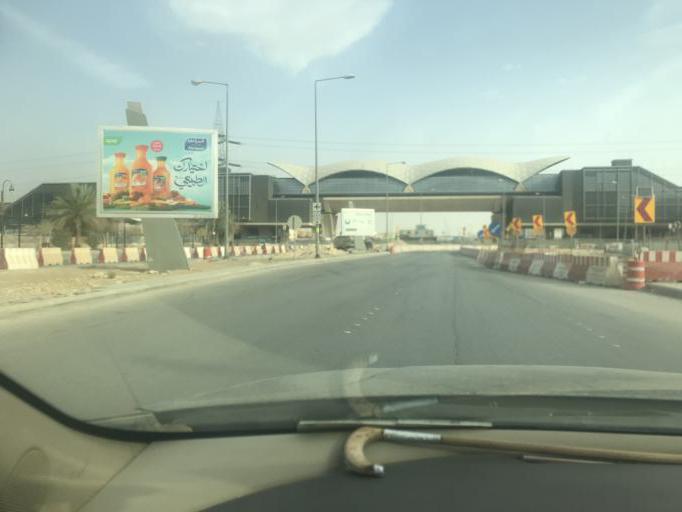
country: SA
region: Ar Riyad
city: Riyadh
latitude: 24.8028
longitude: 46.6953
